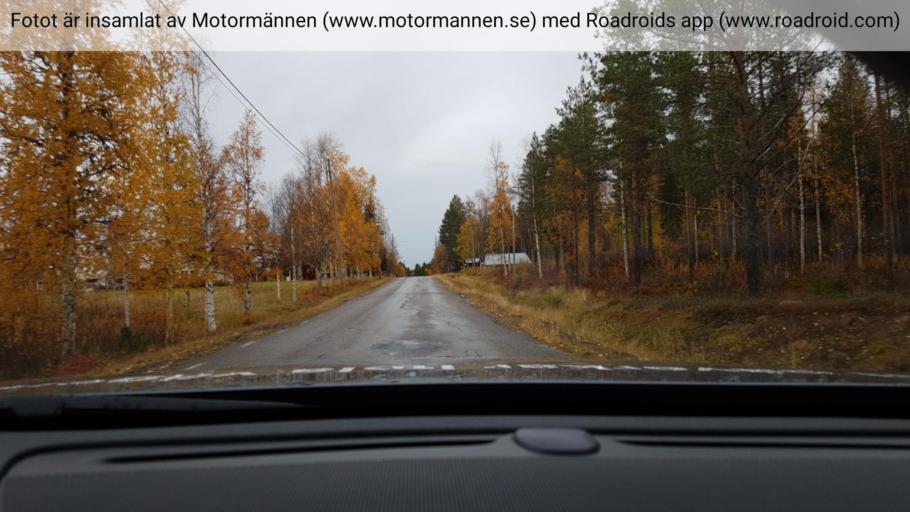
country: SE
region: Norrbotten
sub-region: Pajala Kommun
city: Pajala
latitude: 67.1574
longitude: 22.6563
